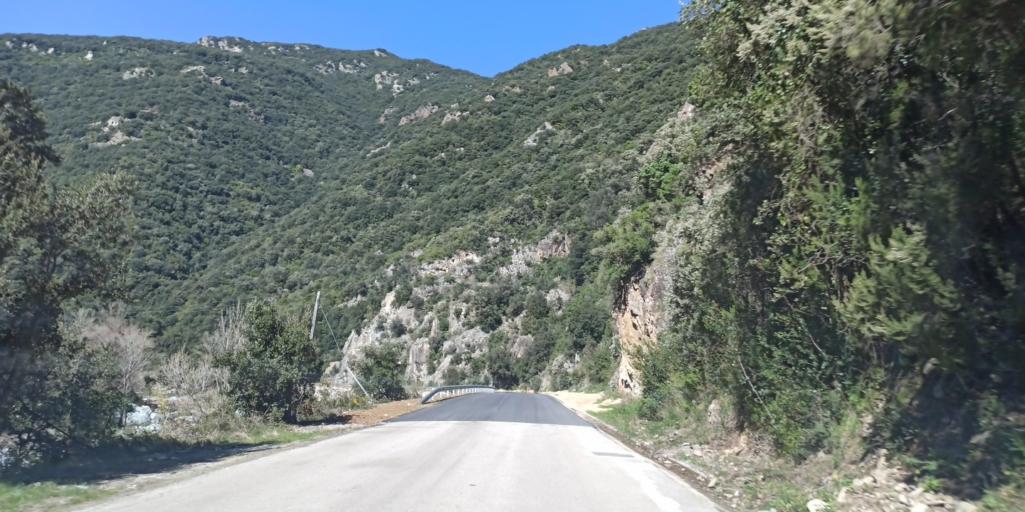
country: ES
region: Catalonia
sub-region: Provincia de Girona
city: Susqueda
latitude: 41.9901
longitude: 2.5702
